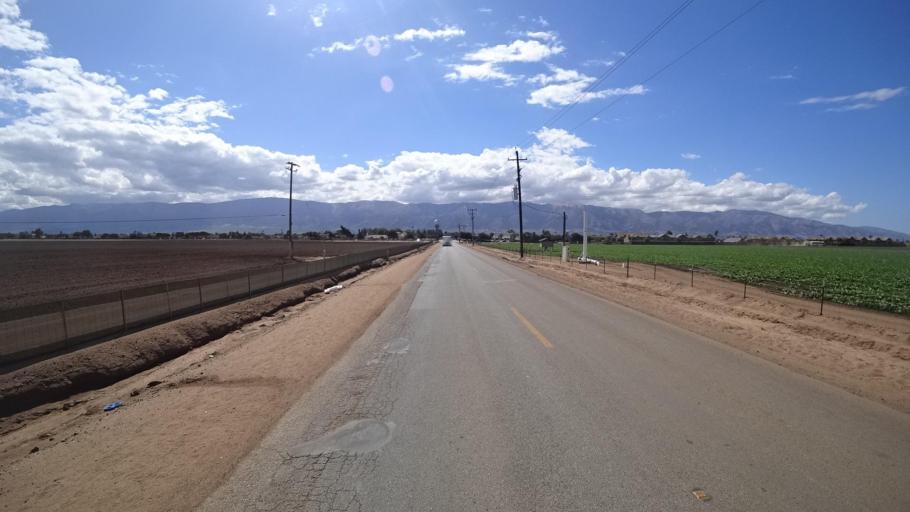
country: US
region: California
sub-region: Monterey County
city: Gonzales
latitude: 36.5161
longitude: -121.4318
